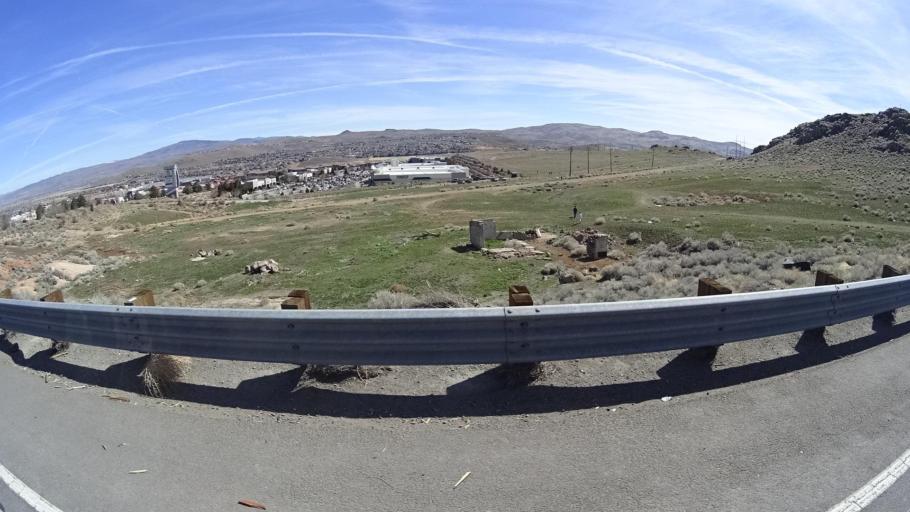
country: US
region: Nevada
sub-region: Washoe County
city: Sun Valley
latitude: 39.5750
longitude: -119.7459
